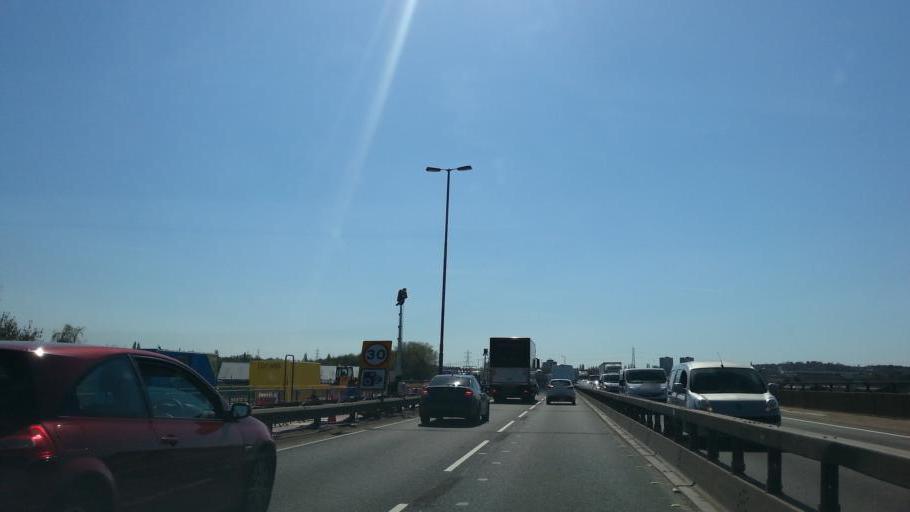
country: GB
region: England
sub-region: Sandwell
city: Oldbury
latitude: 52.4987
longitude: -2.0134
